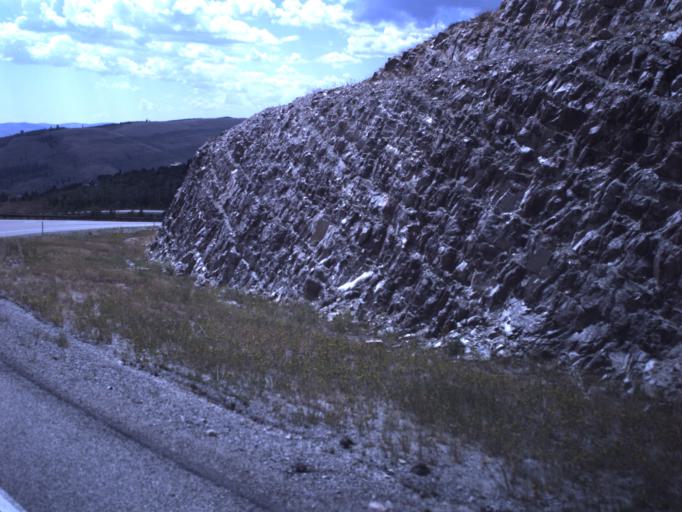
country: US
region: Idaho
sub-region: Bear Lake County
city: Paris
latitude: 41.9314
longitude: -111.4338
